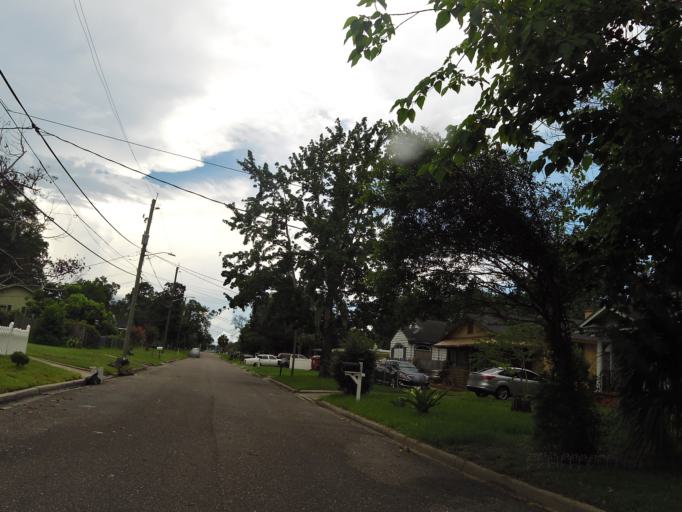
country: US
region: Florida
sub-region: Duval County
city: Jacksonville
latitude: 30.3719
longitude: -81.6487
